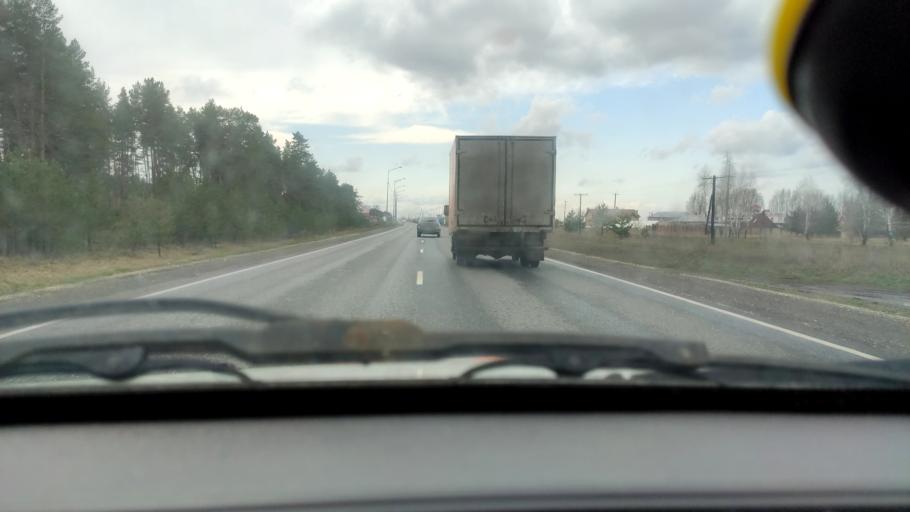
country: RU
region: Samara
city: Povolzhskiy
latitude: 53.5941
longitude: 49.5842
